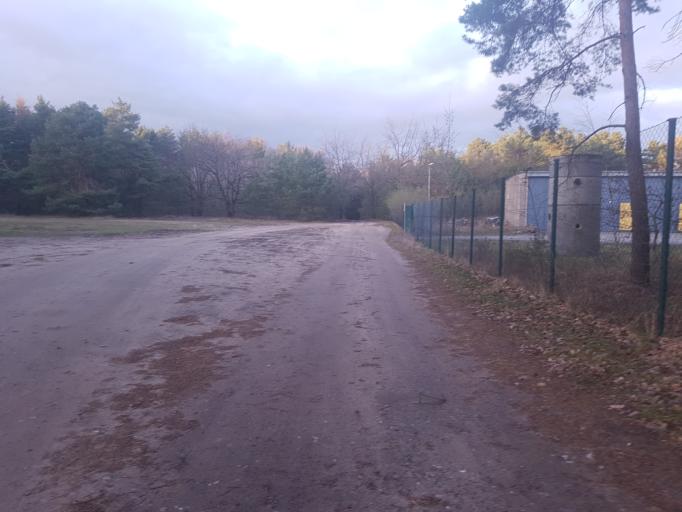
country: DE
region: Brandenburg
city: Eisenhuettenstadt
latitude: 52.1602
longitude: 14.6642
